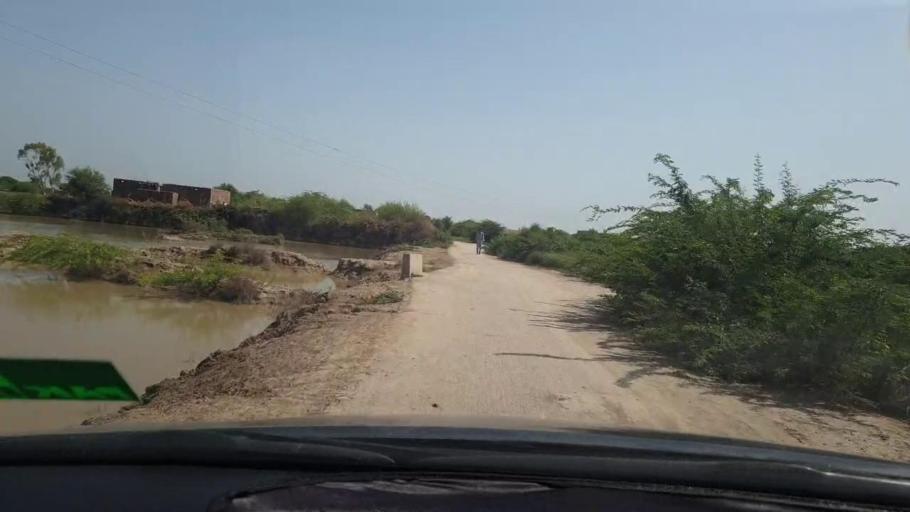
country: PK
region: Sindh
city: Digri
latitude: 24.9417
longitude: 69.1866
